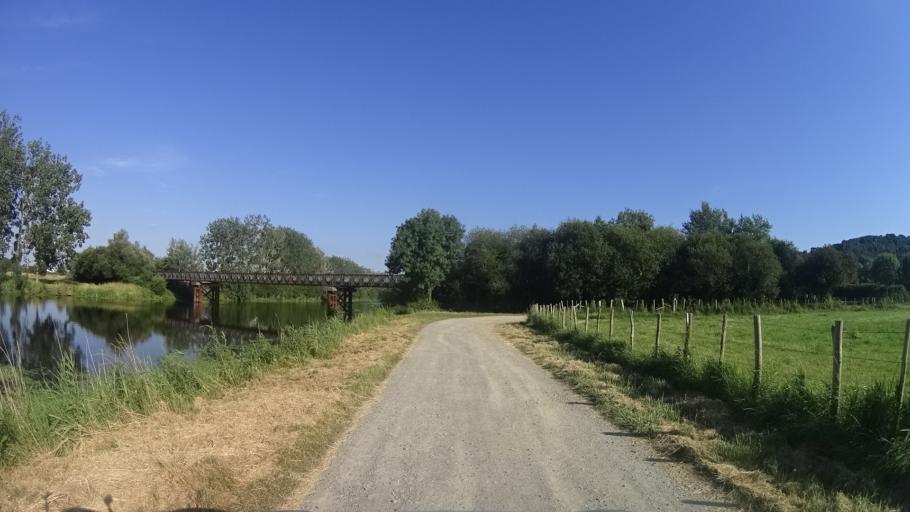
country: FR
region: Brittany
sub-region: Departement du Morbihan
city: Saint-Jean-la-Poterie
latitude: 47.6424
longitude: -2.1091
